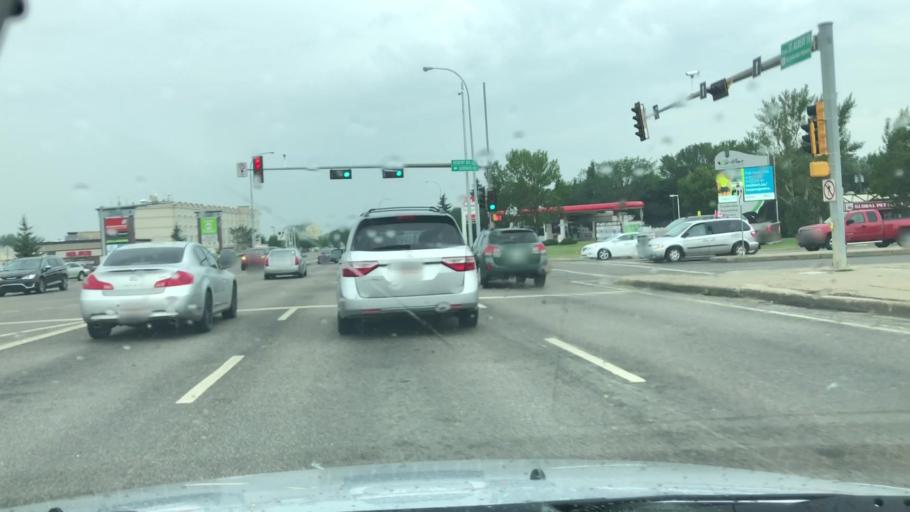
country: CA
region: Alberta
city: St. Albert
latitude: 53.6213
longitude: -113.6091
